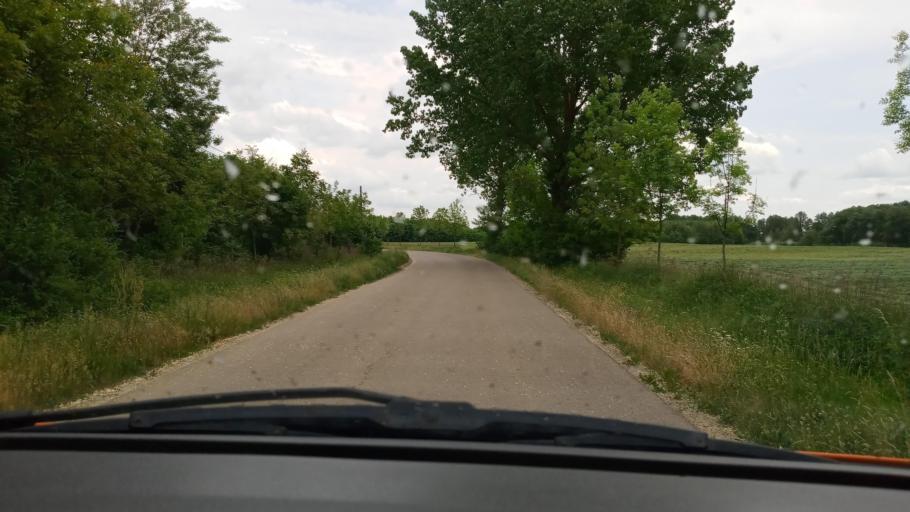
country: HU
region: Baranya
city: Vajszlo
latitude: 45.8288
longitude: 17.9749
